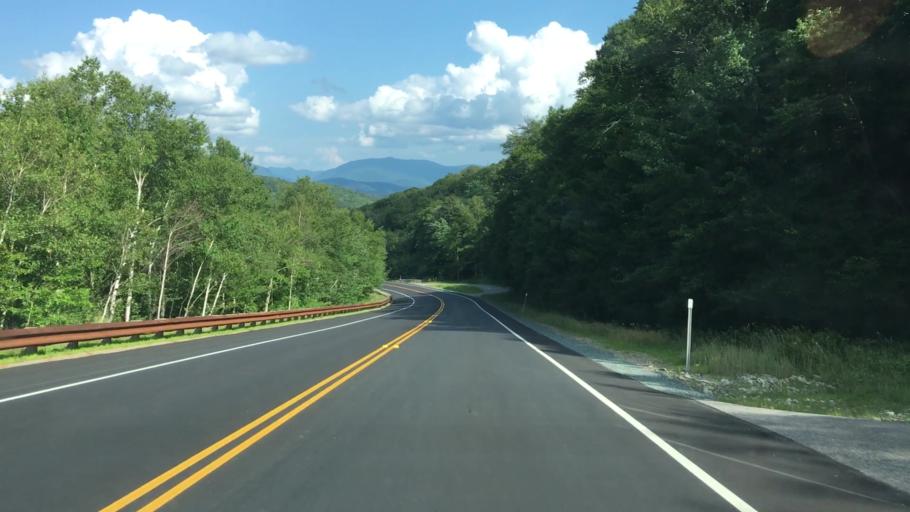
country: US
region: New Hampshire
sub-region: Grafton County
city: Woodstock
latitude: 44.0352
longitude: -71.7778
